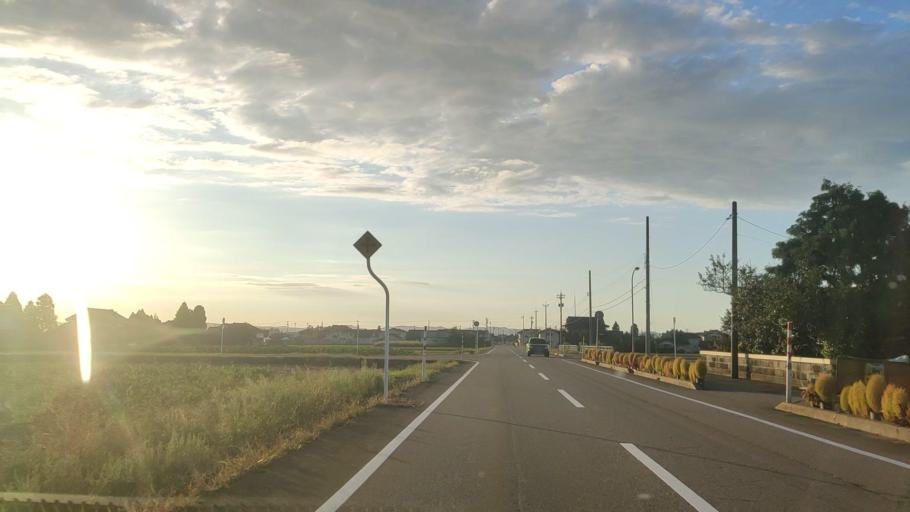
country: JP
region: Toyama
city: Nanto-shi
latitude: 36.5950
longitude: 136.9503
